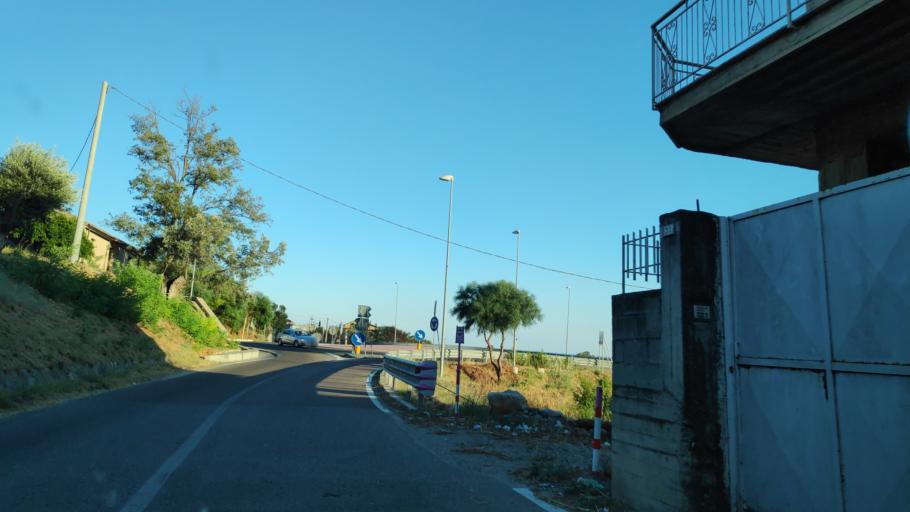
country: IT
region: Calabria
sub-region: Provincia di Reggio Calabria
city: Locri
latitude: 38.2369
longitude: 16.2377
